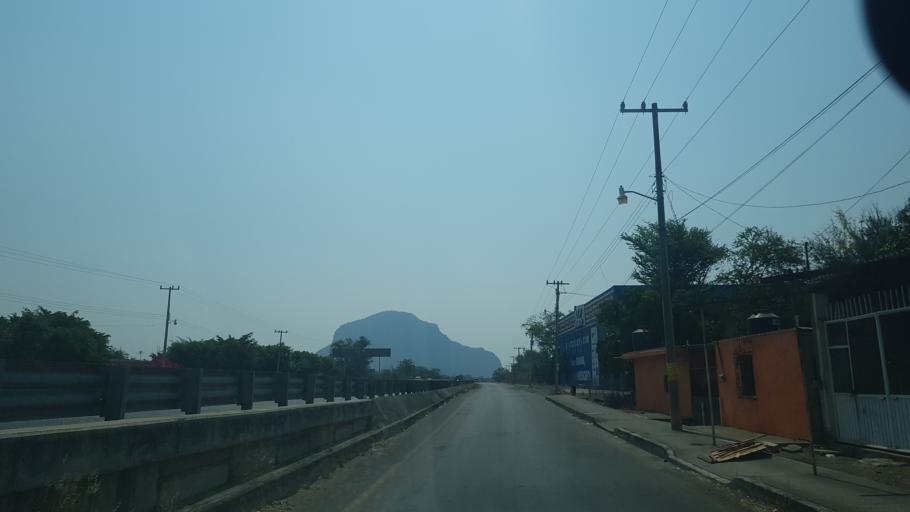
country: MX
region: Morelos
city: Amayuca
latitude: 18.7166
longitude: -98.7925
